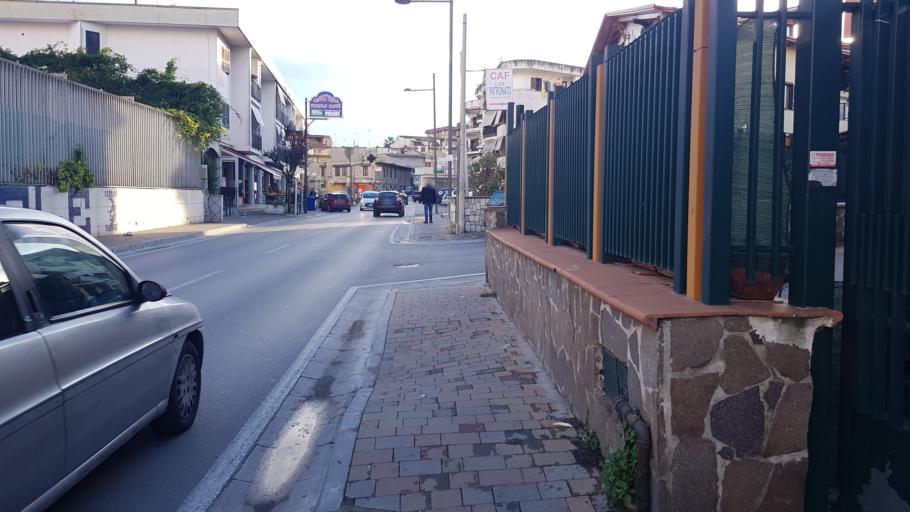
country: IT
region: Campania
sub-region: Provincia di Napoli
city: Mugnano di Napoli
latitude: 40.9091
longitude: 14.2121
